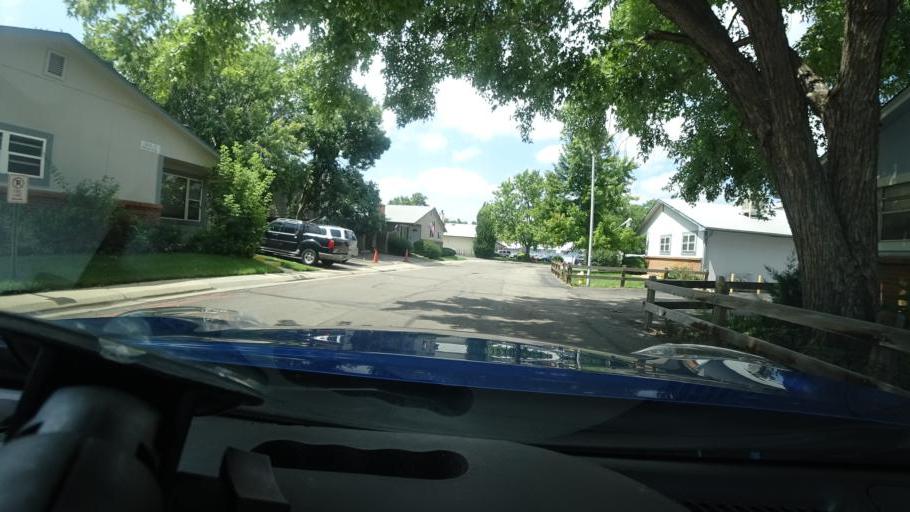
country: US
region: Colorado
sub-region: Adams County
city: Aurora
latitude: 39.7168
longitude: -104.8524
